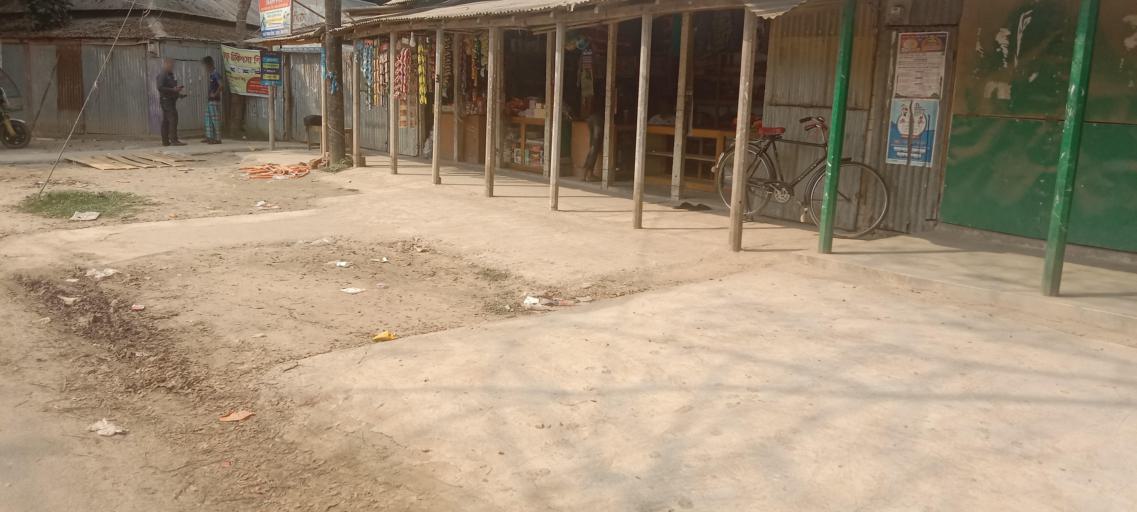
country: BD
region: Dhaka
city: Sakhipur
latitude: 24.3341
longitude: 90.2869
